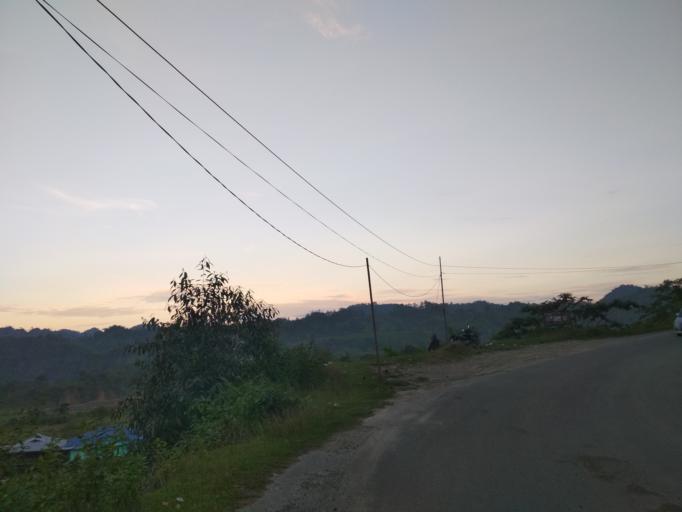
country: IN
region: Arunachal Pradesh
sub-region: Papum Pare
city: Naharlagun
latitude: 27.0884
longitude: 93.6693
